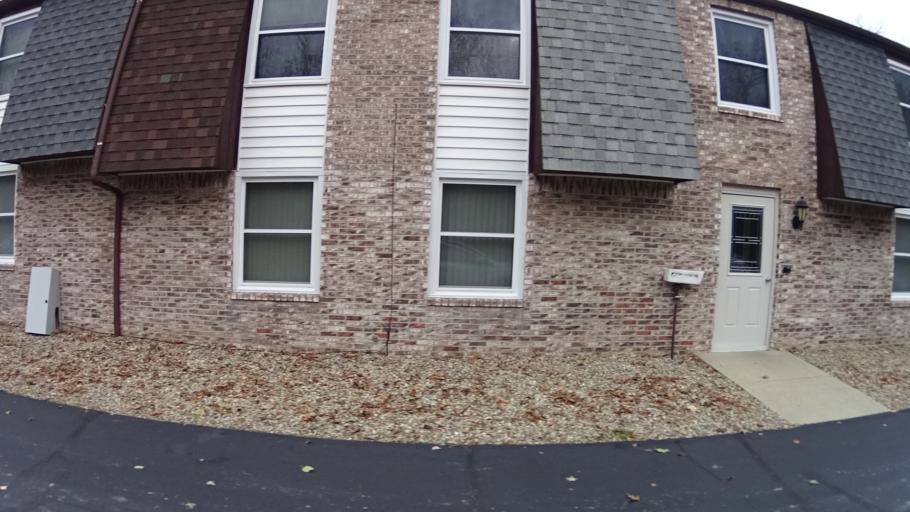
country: US
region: Ohio
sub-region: Lorain County
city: Elyria
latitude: 41.3304
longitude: -82.0736
